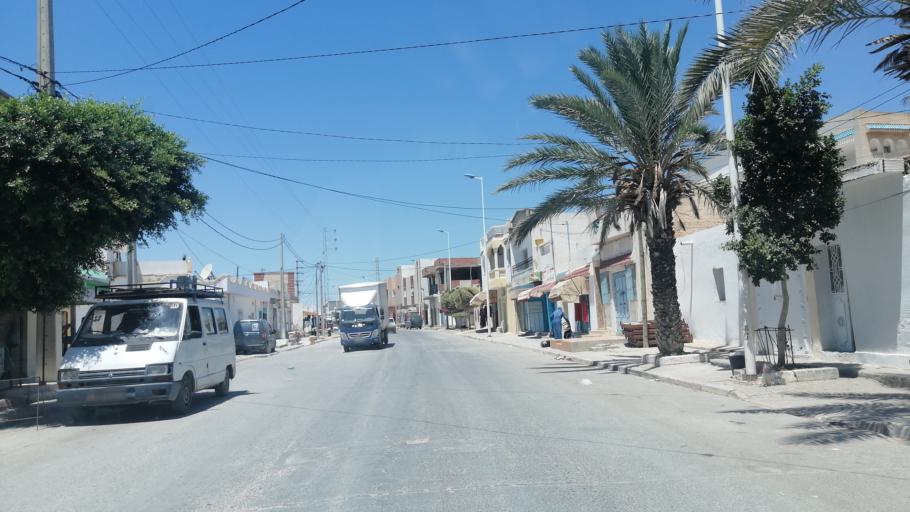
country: TN
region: Al Qayrawan
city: Sbikha
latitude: 36.1208
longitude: 10.0955
